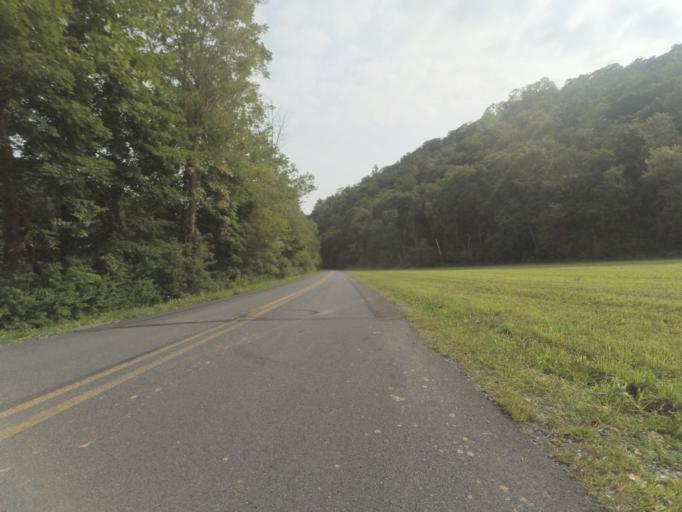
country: US
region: Pennsylvania
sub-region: Huntingdon County
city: Huntingdon
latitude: 40.5404
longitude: -78.0707
